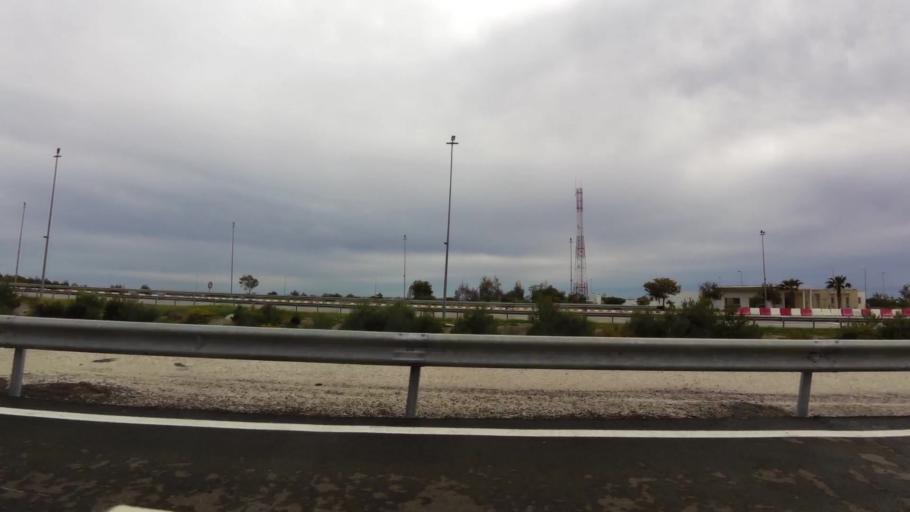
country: ES
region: Ceuta
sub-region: Ceuta
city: Ceuta
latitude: 35.7455
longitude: -5.3542
